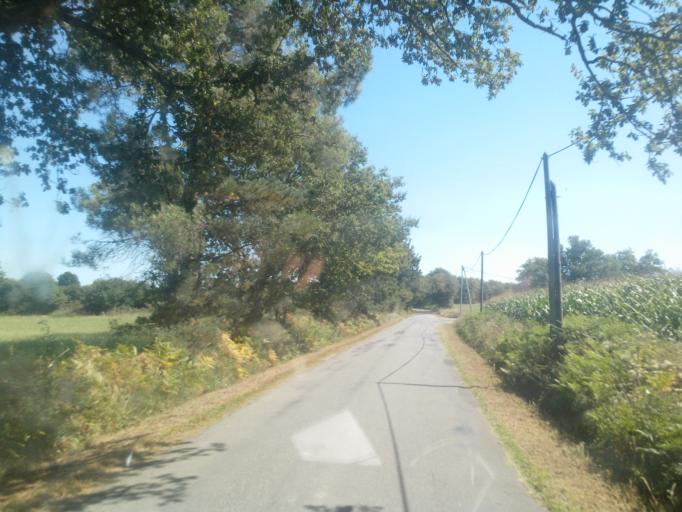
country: FR
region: Brittany
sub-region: Departement du Morbihan
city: Molac
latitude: 47.7317
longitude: -2.4138
